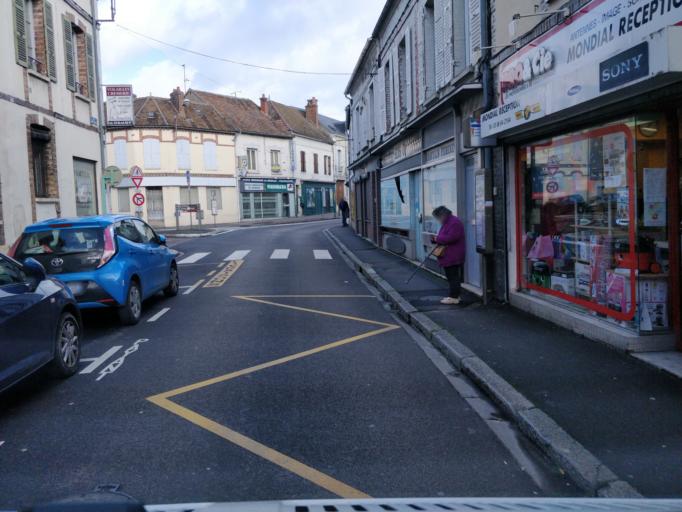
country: FR
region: Bourgogne
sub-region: Departement de l'Yonne
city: Sens
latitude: 48.1977
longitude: 3.2719
